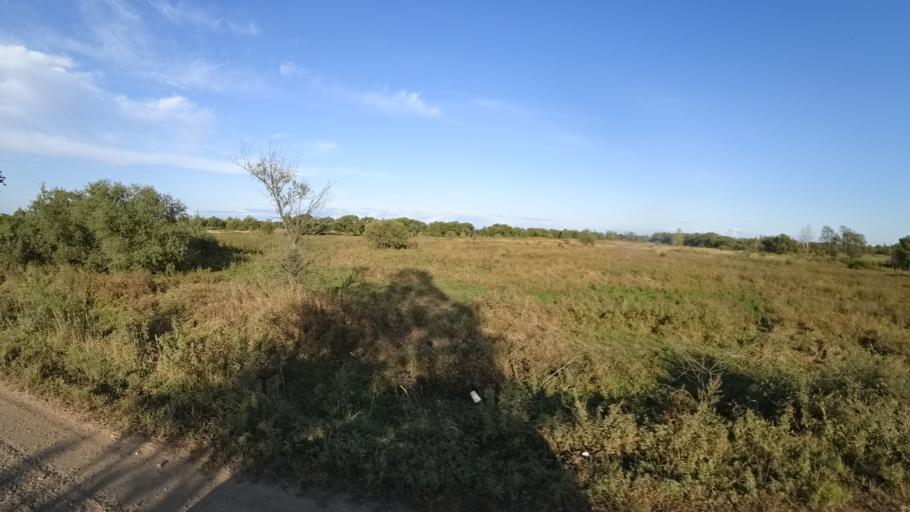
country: RU
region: Amur
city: Arkhara
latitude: 49.3621
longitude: 130.1367
